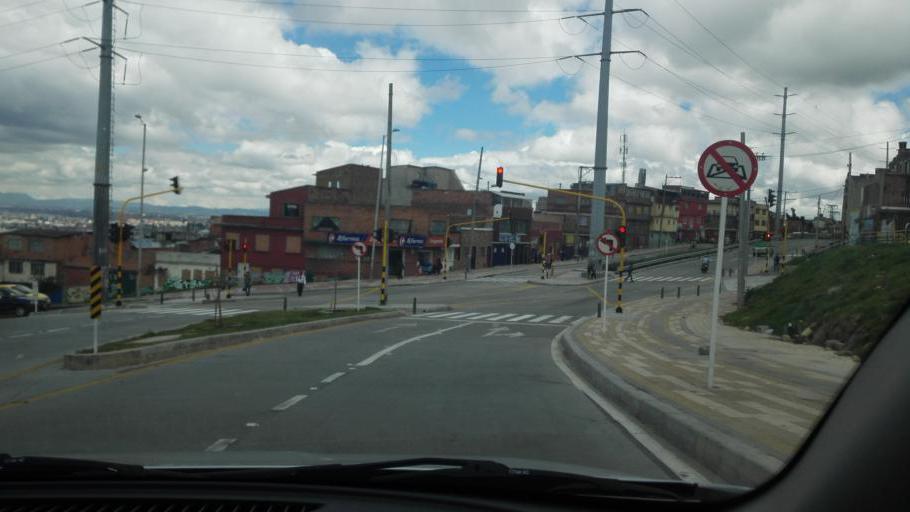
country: CO
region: Bogota D.C.
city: Bogota
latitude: 4.5894
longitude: -74.0714
